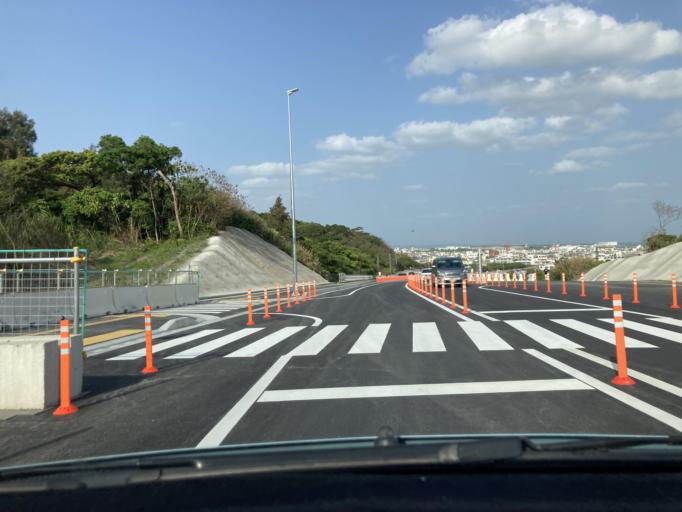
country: JP
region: Okinawa
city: Ginowan
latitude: 26.2098
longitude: 127.7541
